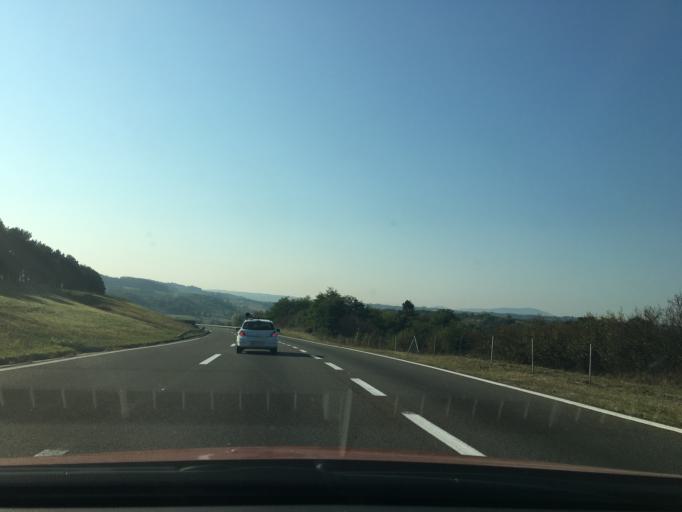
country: RS
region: Central Serbia
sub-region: Belgrade
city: Grocka
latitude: 44.6198
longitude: 20.6387
